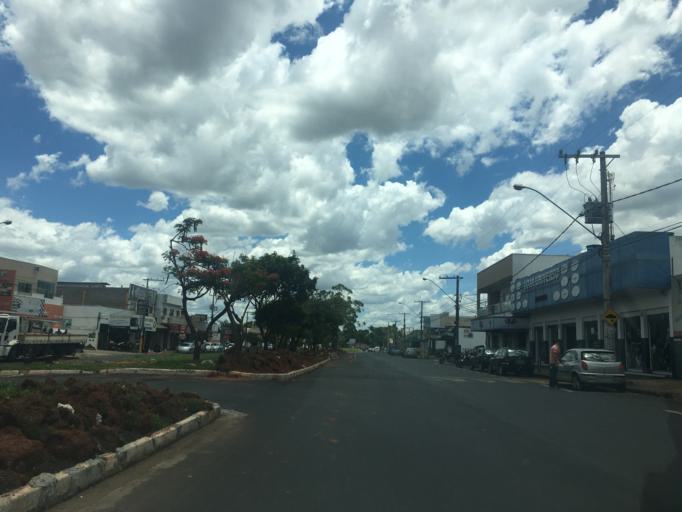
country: BR
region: Minas Gerais
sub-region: Uberlandia
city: Uberlandia
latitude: -18.9454
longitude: -48.3115
